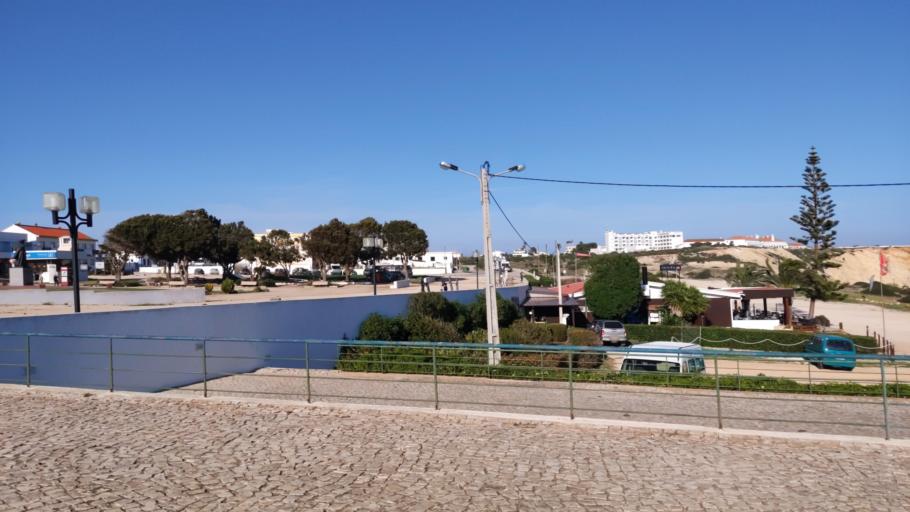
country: PT
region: Faro
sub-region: Vila do Bispo
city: Sagres
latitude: 37.0071
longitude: -8.9412
